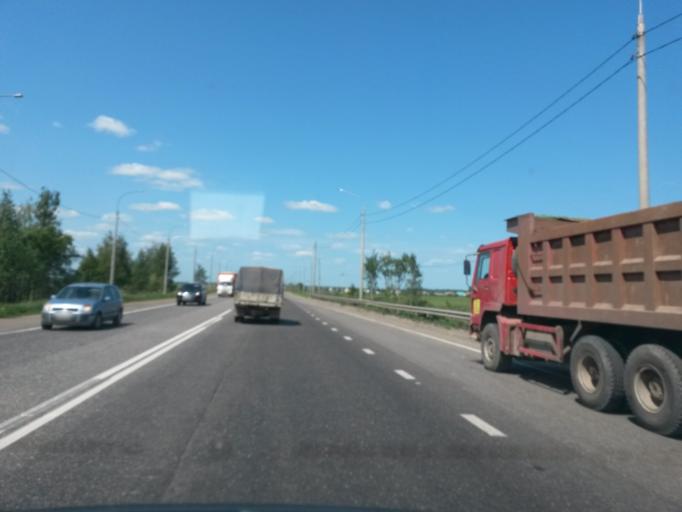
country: RU
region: Jaroslavl
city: Yaroslavl
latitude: 57.6225
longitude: 39.7699
